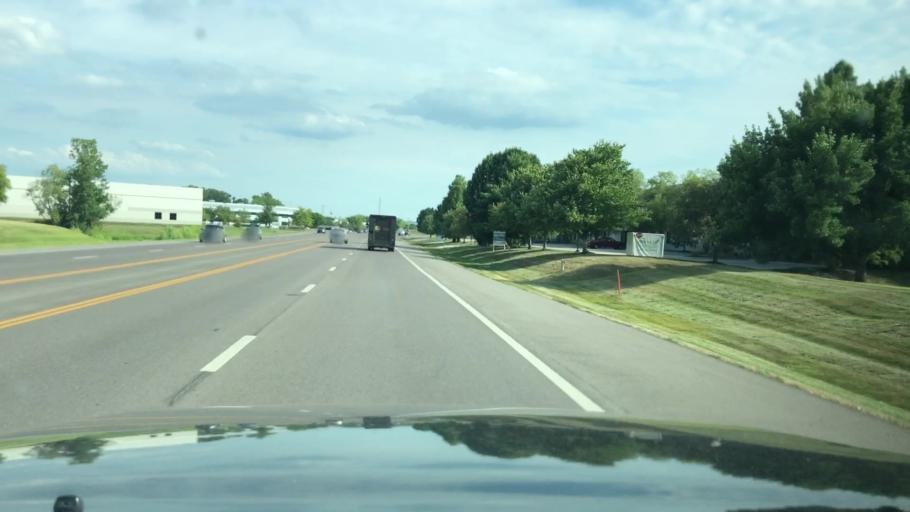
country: US
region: Missouri
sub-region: Saint Charles County
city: Saint Charles
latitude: 38.7844
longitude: -90.4594
